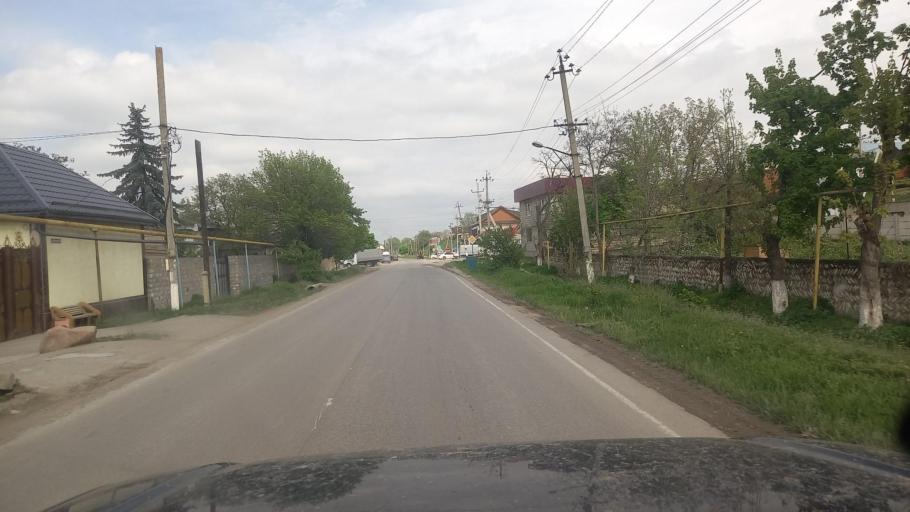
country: RU
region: Kabardino-Balkariya
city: Sarmakovo
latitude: 43.7461
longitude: 43.2061
